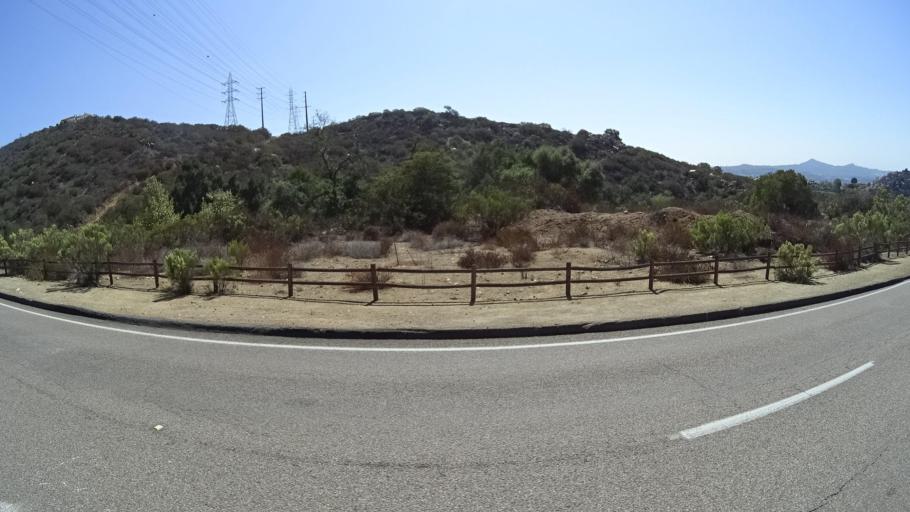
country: US
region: California
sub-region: San Diego County
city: Granite Hills
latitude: 32.8102
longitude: -116.8929
